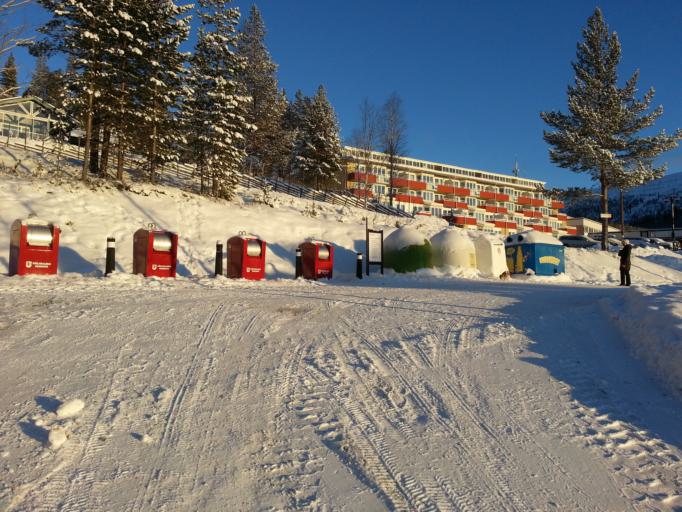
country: SE
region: Jaemtland
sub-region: Harjedalens Kommun
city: Sveg
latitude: 62.4235
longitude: 13.9528
